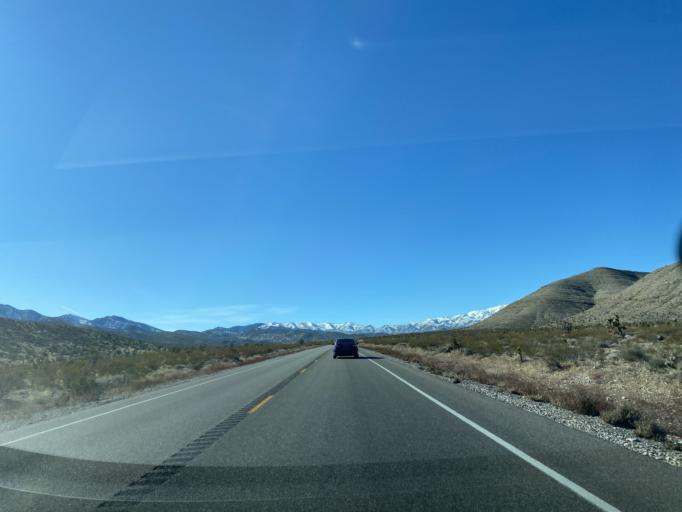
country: US
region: Nevada
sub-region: Clark County
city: Summerlin South
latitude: 36.2880
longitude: -115.4318
